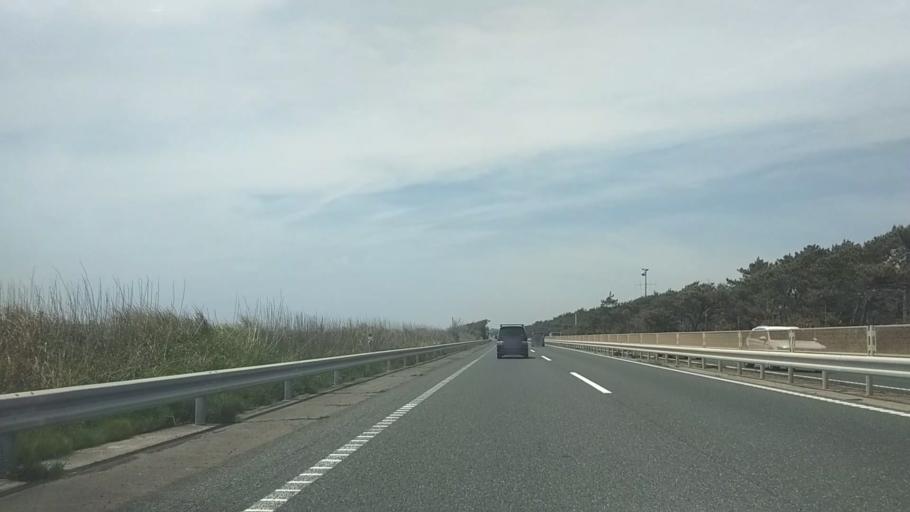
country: JP
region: Shizuoka
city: Kosai-shi
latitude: 34.6805
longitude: 137.5610
